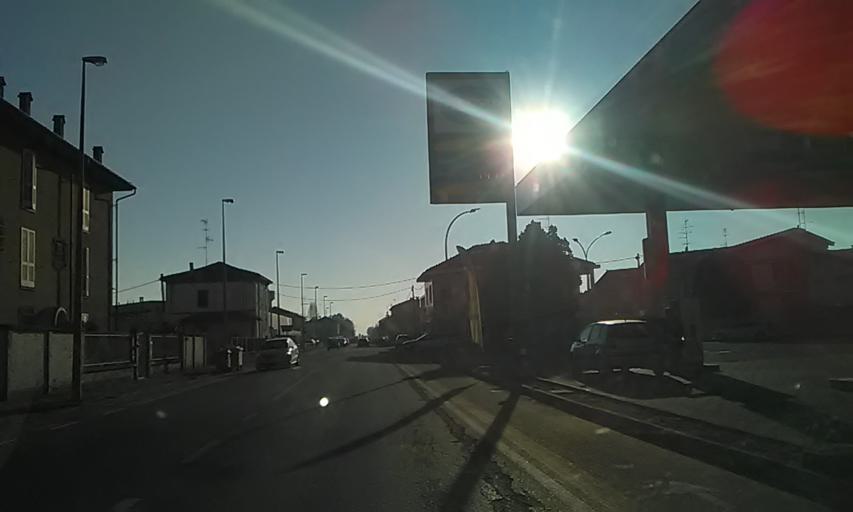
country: IT
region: Piedmont
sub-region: Provincia di Vercelli
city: Vercelli
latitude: 45.3159
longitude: 8.4096
